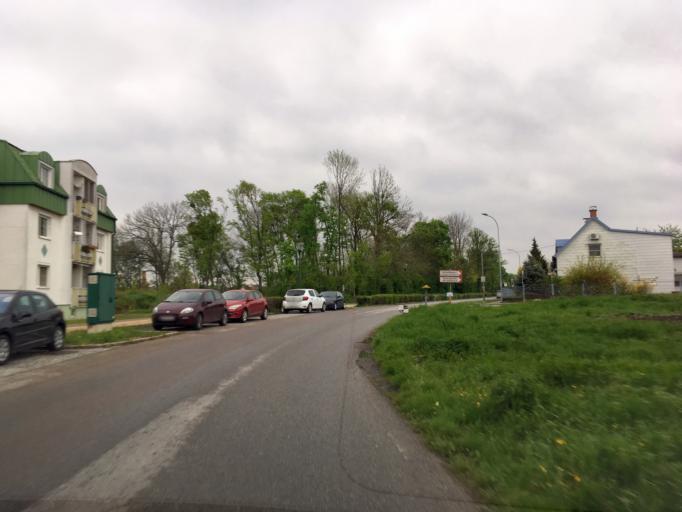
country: AT
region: Lower Austria
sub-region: Politischer Bezirk Bruck an der Leitha
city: Bruck an der Leitha
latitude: 48.0154
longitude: 16.7739
